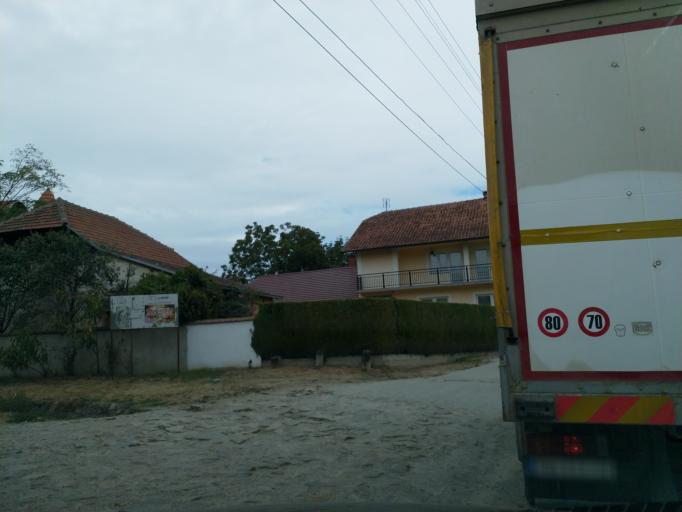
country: RS
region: Central Serbia
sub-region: Pomoravski Okrug
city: Cuprija
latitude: 43.8671
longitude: 21.3216
